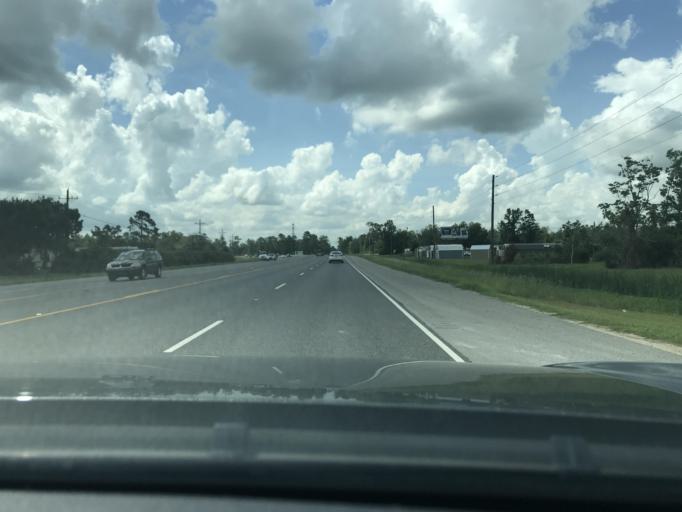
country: US
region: Louisiana
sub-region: Calcasieu Parish
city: Moss Bluff
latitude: 30.3227
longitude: -93.2003
